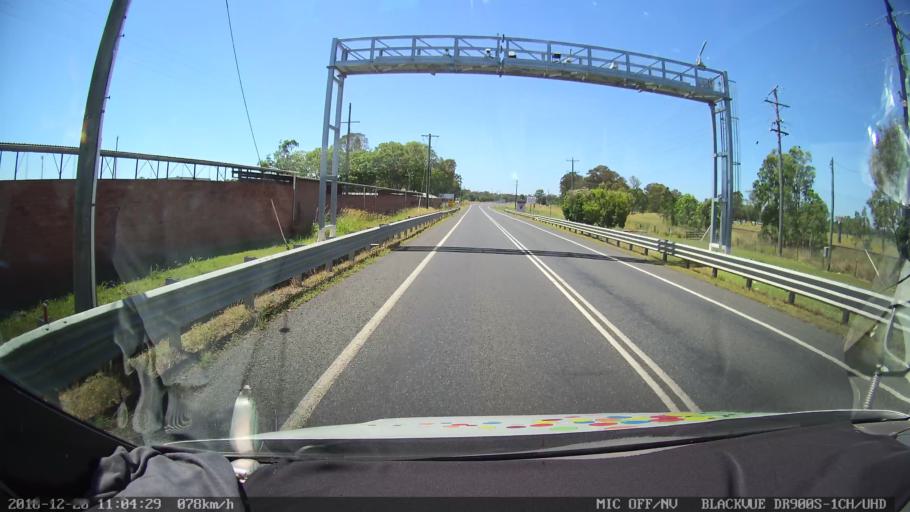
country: AU
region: New South Wales
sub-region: Richmond Valley
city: Casino
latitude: -28.8857
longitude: 153.0457
